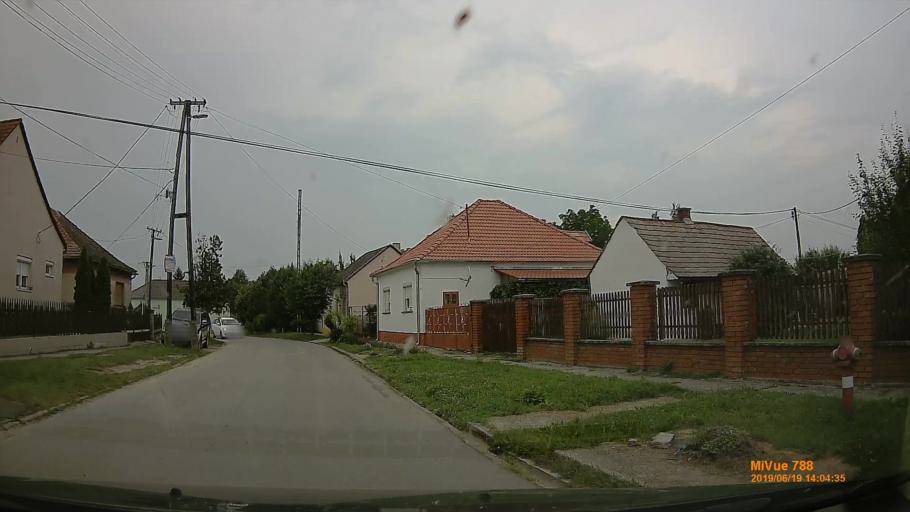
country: HU
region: Baranya
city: Szigetvar
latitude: 46.0552
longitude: 17.8069
